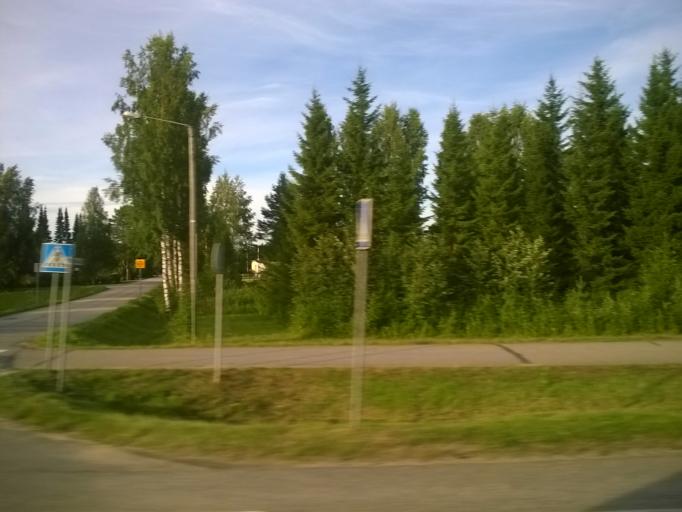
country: FI
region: Kainuu
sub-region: Kajaani
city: Sotkamo
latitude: 64.1285
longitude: 28.4127
